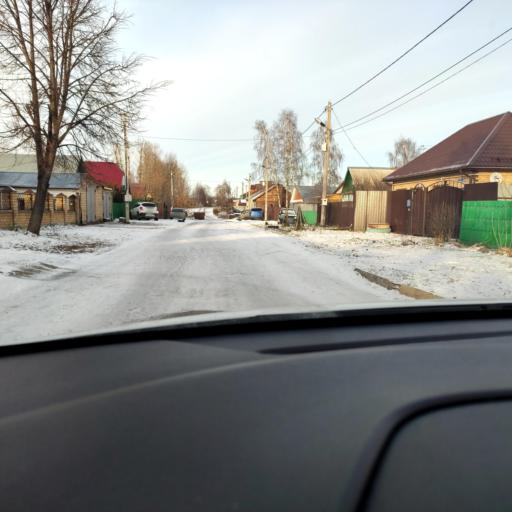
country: RU
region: Tatarstan
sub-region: Gorod Kazan'
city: Kazan
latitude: 55.8729
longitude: 49.0669
